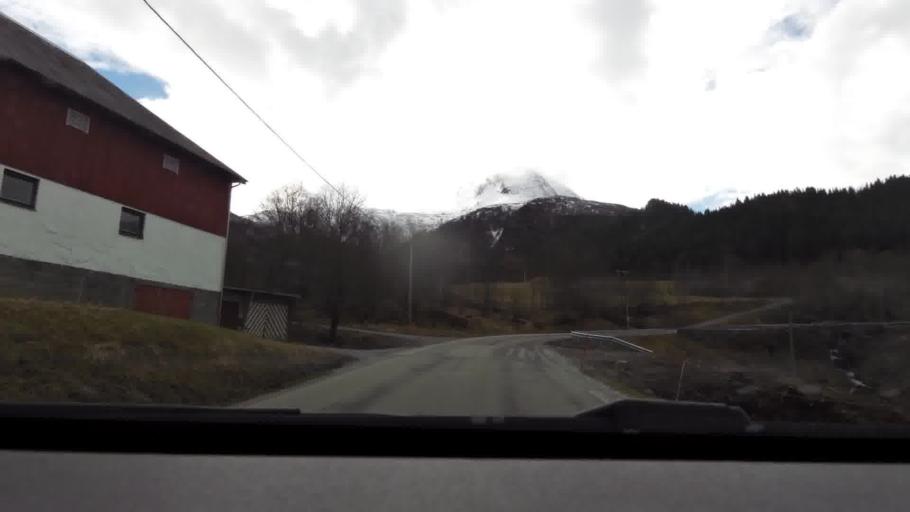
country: NO
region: More og Romsdal
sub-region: Gjemnes
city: Batnfjordsora
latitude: 62.9303
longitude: 7.6055
